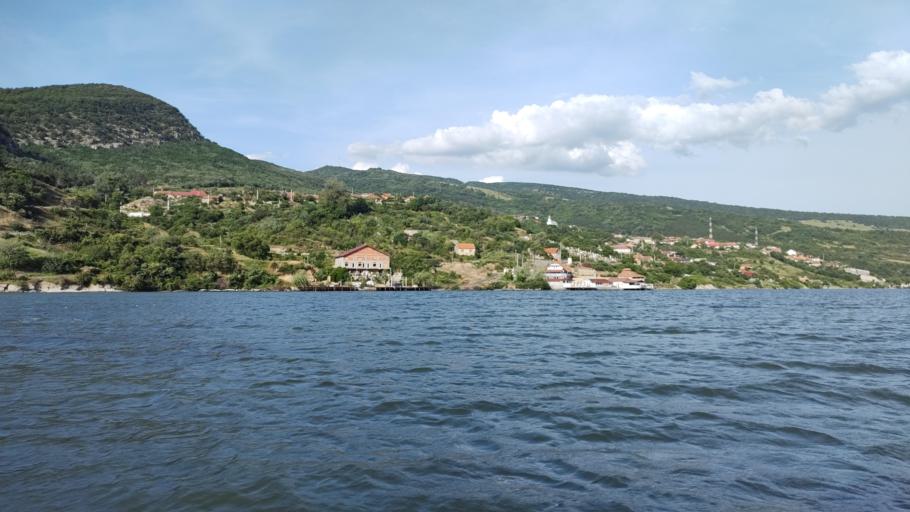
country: RO
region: Mehedinti
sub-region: Comuna Svinita
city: Svinita
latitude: 44.4983
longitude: 22.0918
